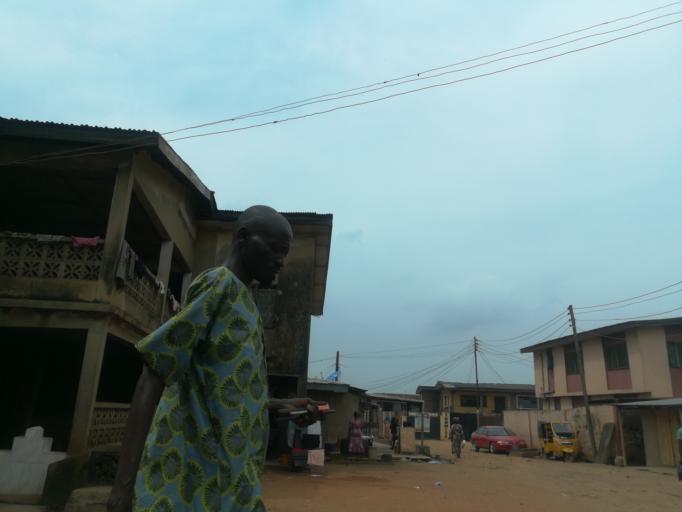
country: NG
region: Oyo
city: Ibadan
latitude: 7.4313
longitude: 3.9196
